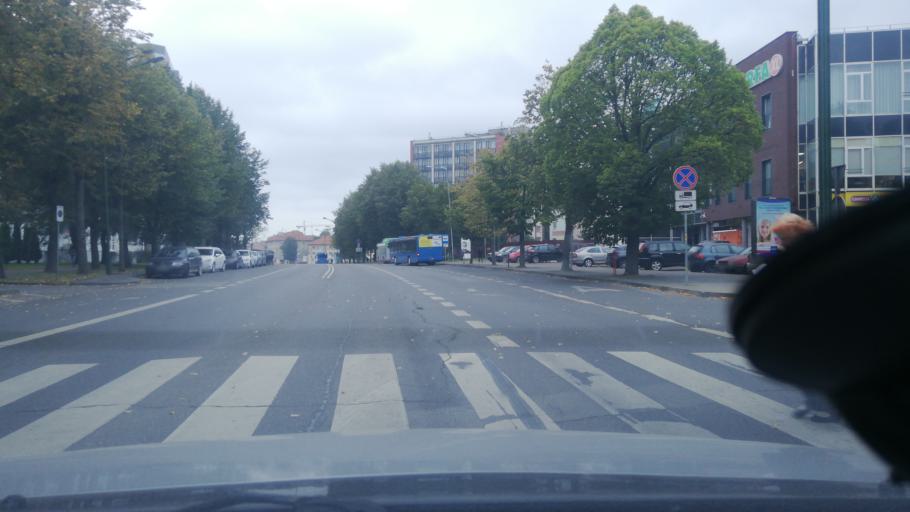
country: LT
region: Klaipedos apskritis
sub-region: Klaipeda
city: Klaipeda
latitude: 55.7048
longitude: 21.1425
